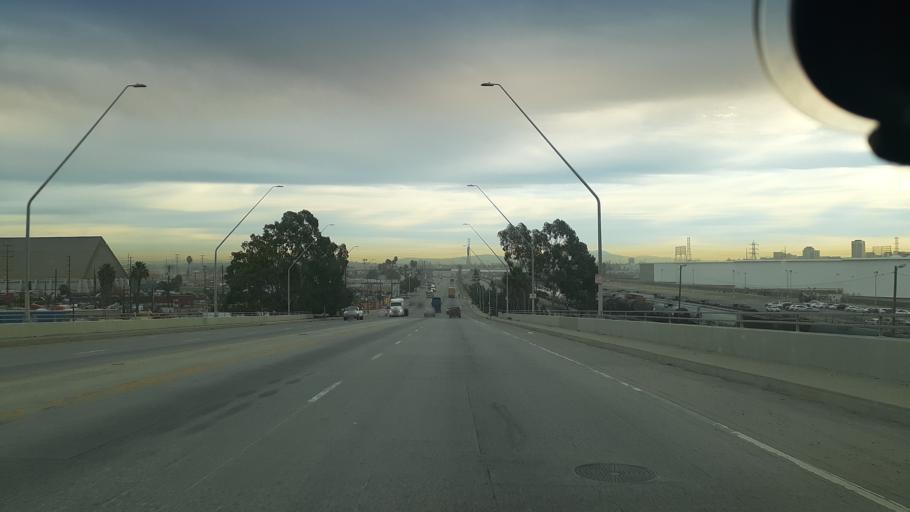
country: US
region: California
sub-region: Los Angeles County
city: Long Beach
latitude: 33.7815
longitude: -118.2366
